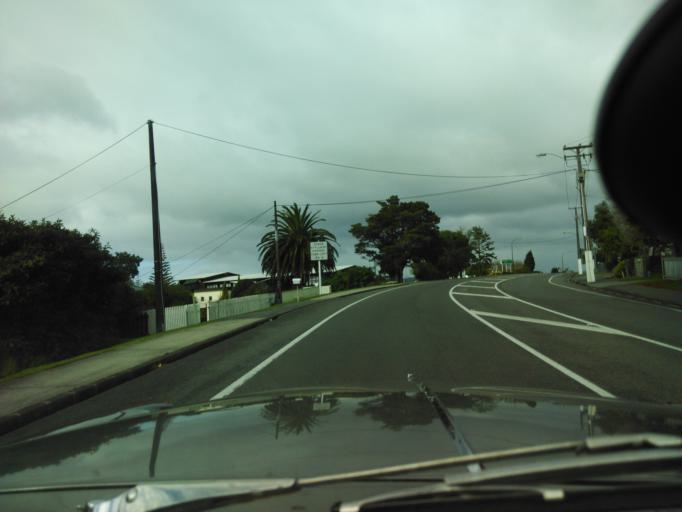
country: NZ
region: Auckland
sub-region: Auckland
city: Wellsford
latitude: -36.2908
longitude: 174.5241
